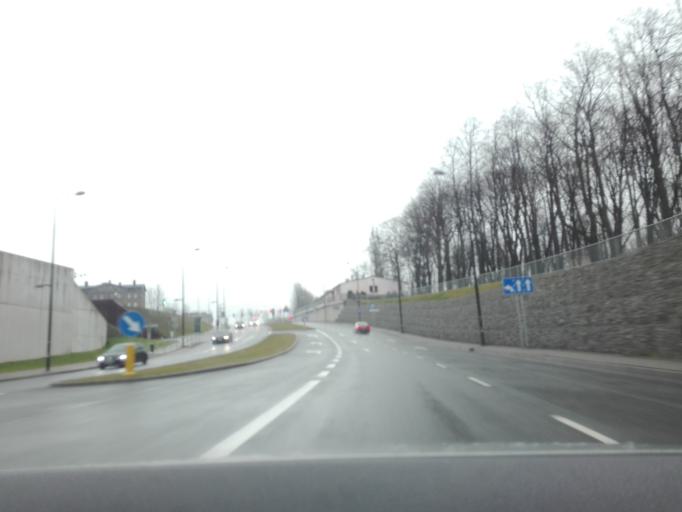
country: PL
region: Silesian Voivodeship
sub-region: Katowice
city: Katowice
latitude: 50.2635
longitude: 19.0360
